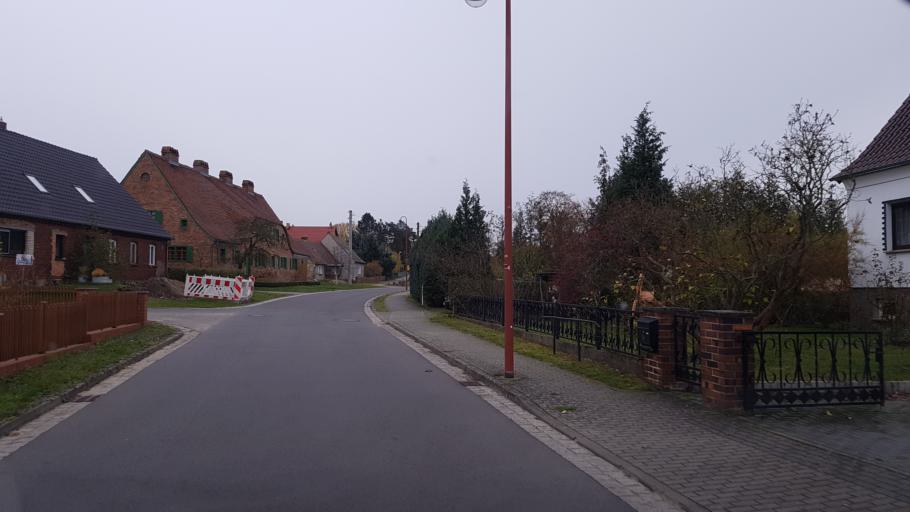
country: DE
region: Brandenburg
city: Crinitz
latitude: 51.7564
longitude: 13.8053
